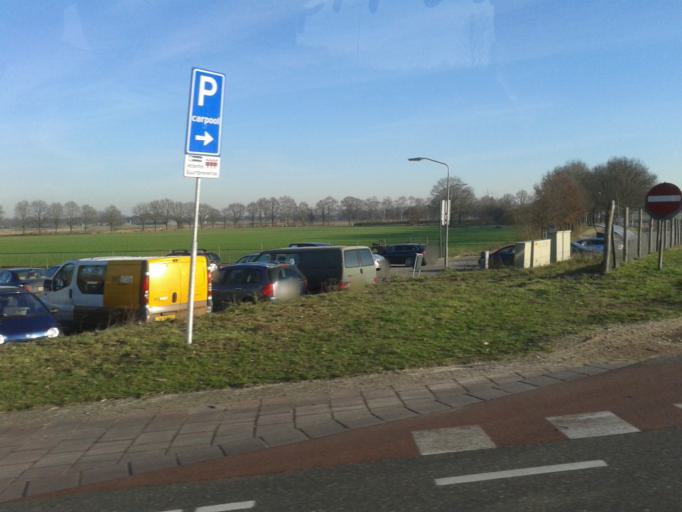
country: NL
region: North Brabant
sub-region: Gemeente Oisterwijk
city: Oisterwijk
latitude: 51.5376
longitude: 5.1794
